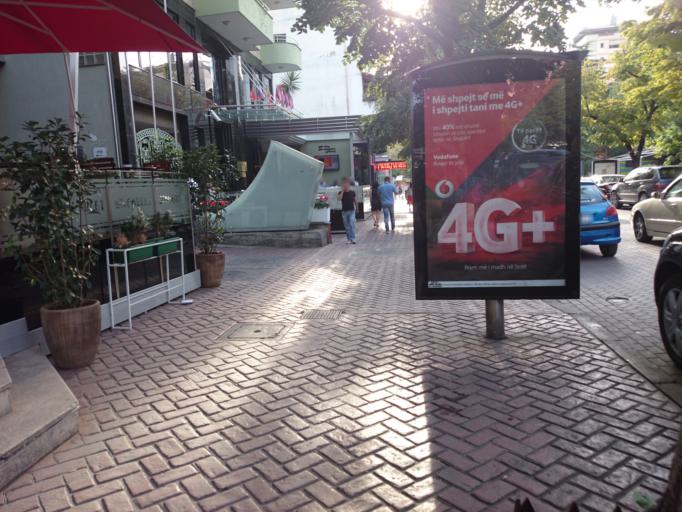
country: AL
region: Tirane
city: Tirana
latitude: 41.3207
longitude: 19.8170
